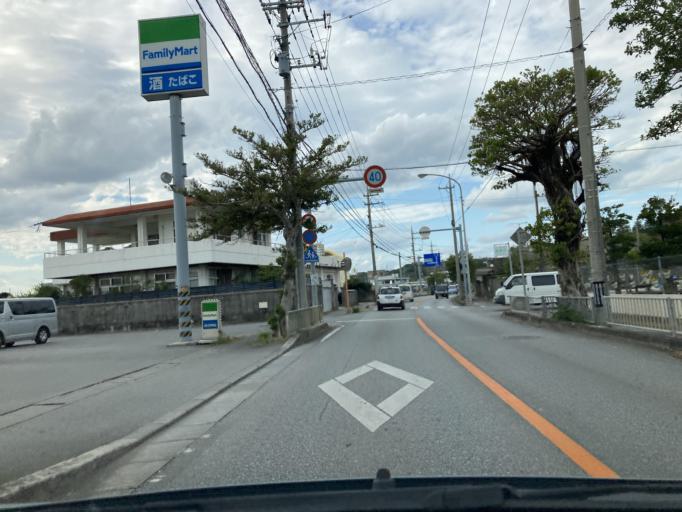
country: JP
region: Okinawa
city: Katsuren-haebaru
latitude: 26.3383
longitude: 127.8730
